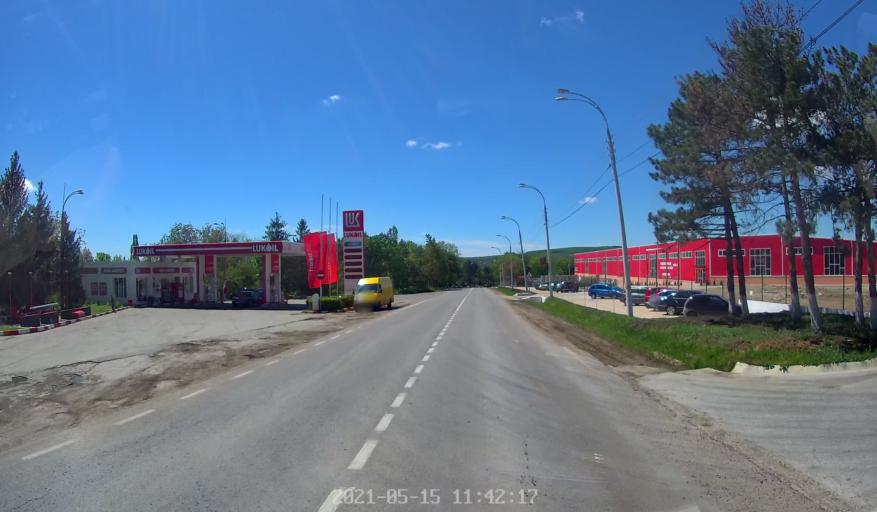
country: MD
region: Hincesti
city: Hincesti
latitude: 46.8342
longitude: 28.6106
